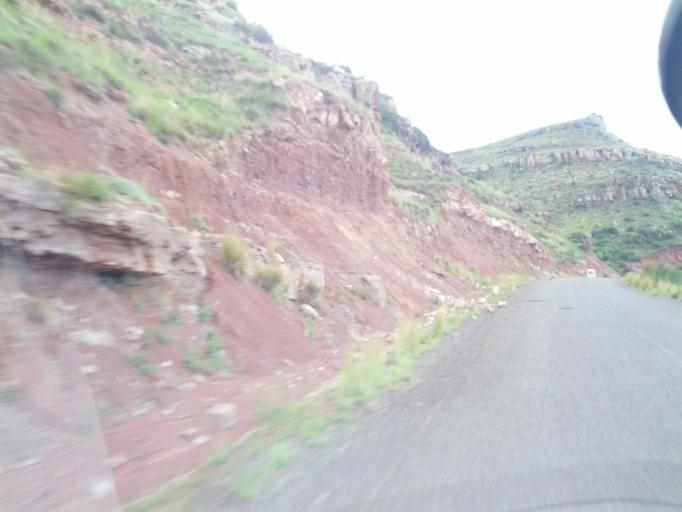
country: LS
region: Qacha's Nek
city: Qacha's Nek
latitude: -30.0604
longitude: 28.5047
